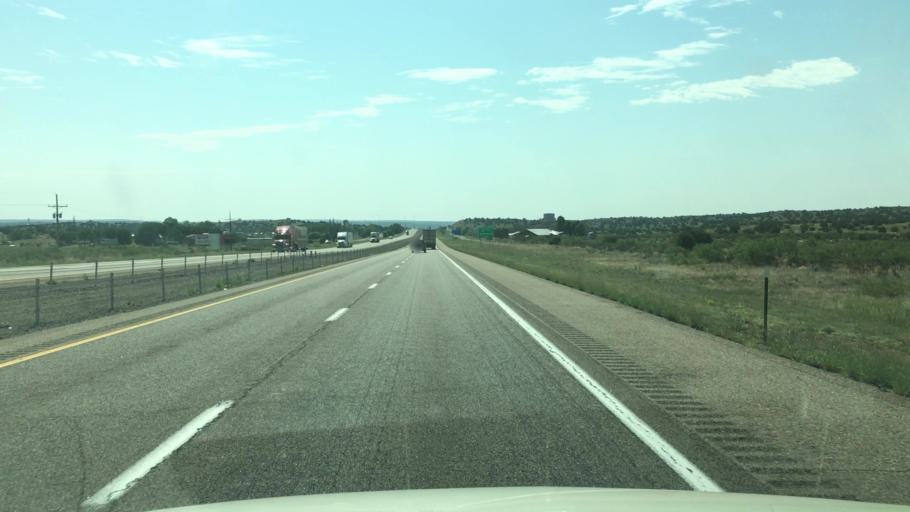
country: US
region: New Mexico
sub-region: Guadalupe County
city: Santa Rosa
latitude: 34.9577
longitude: -104.7288
